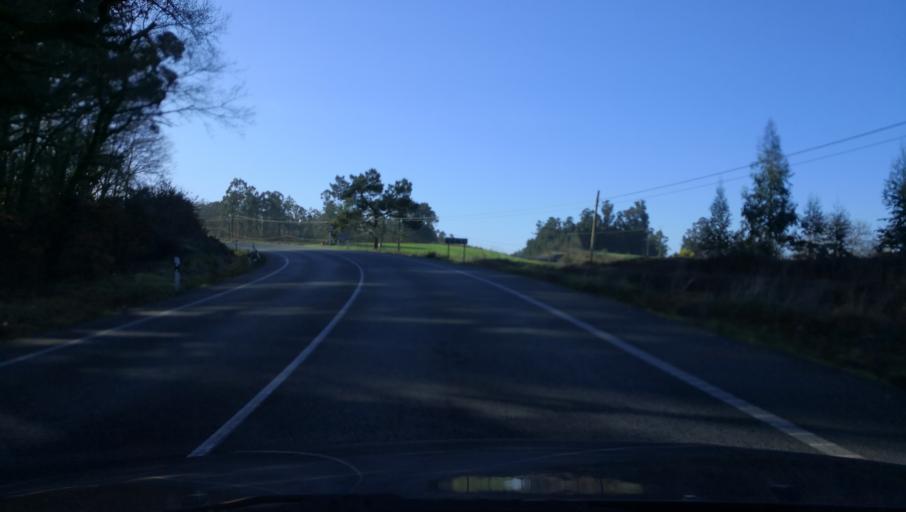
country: ES
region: Galicia
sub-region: Provincia da Coruna
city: Vedra
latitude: 42.8112
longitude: -8.4799
